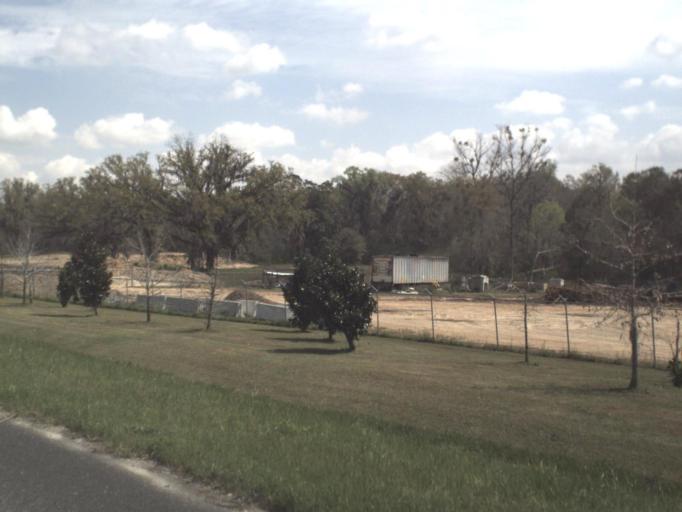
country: US
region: Florida
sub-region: Gadsden County
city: Havana
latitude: 30.6615
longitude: -84.4112
